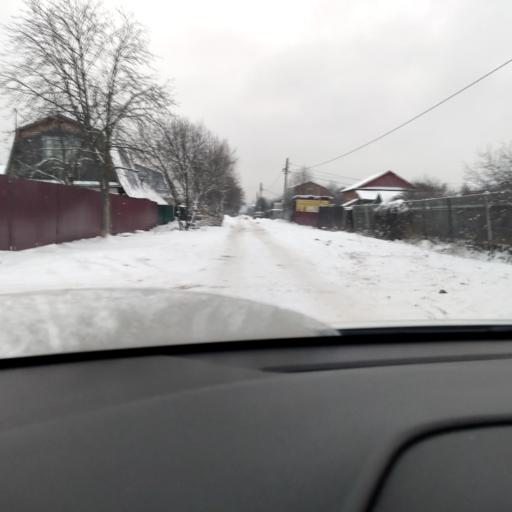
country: RU
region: Tatarstan
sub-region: Gorod Kazan'
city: Kazan
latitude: 55.8389
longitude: 49.2158
